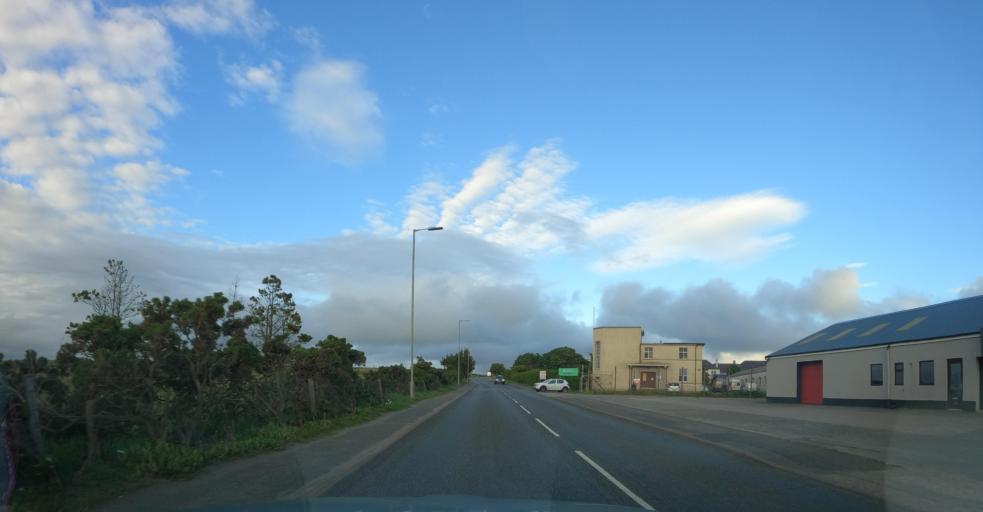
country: GB
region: Scotland
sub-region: Eilean Siar
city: Stornoway
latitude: 58.2083
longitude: -6.3710
